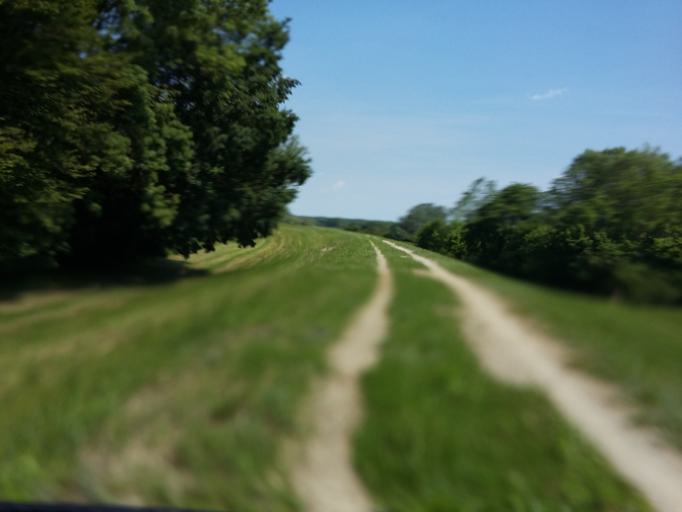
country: AT
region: Lower Austria
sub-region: Politischer Bezirk Ganserndorf
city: Angern an der March
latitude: 48.4162
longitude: 16.8630
